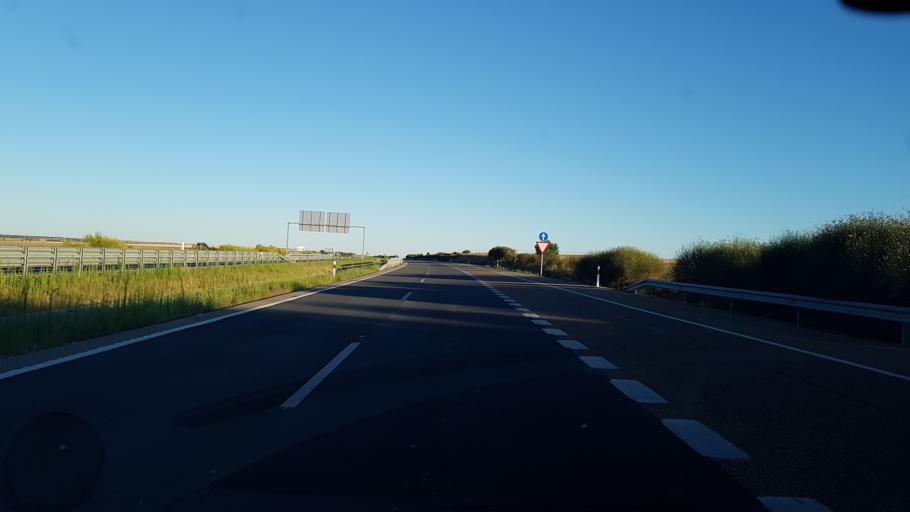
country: ES
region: Castille and Leon
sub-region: Provincia de Zamora
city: Toro
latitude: 41.5455
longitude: -5.3793
